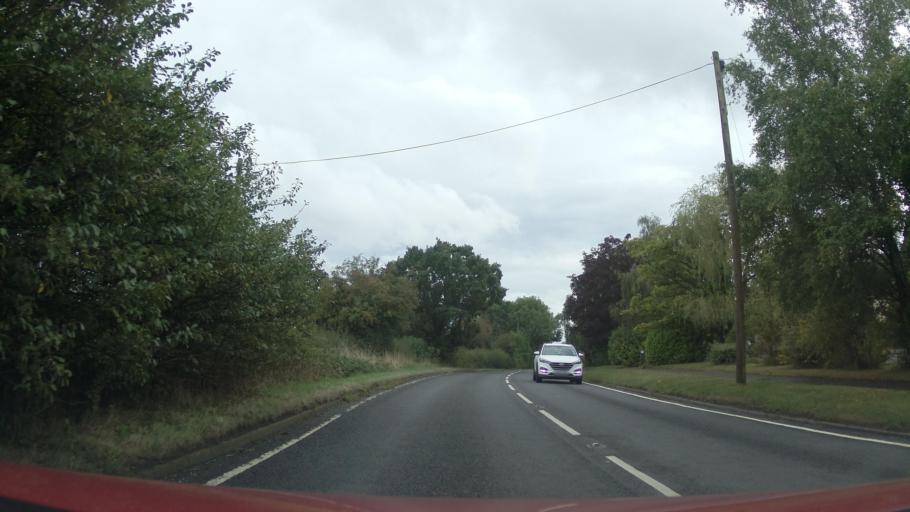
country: GB
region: England
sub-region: Worcestershire
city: Droitwich
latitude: 52.3134
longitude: -2.1771
